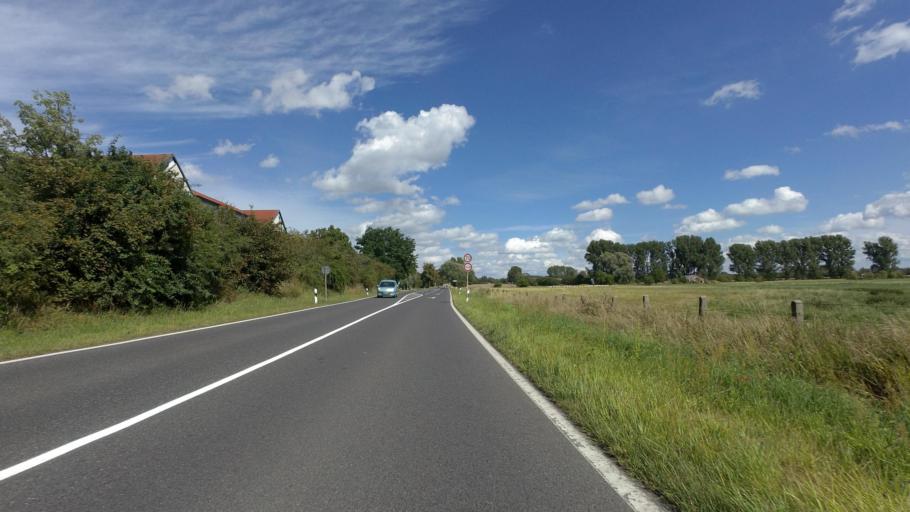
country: DE
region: Brandenburg
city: Wustermark
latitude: 52.5409
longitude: 12.9344
